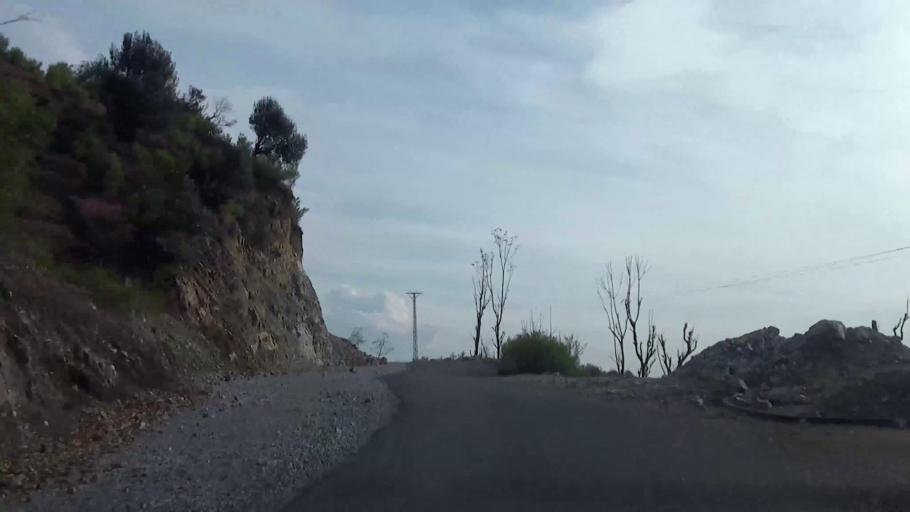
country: PK
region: Azad Kashmir
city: Muzaffarabad
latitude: 34.3622
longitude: 73.5060
